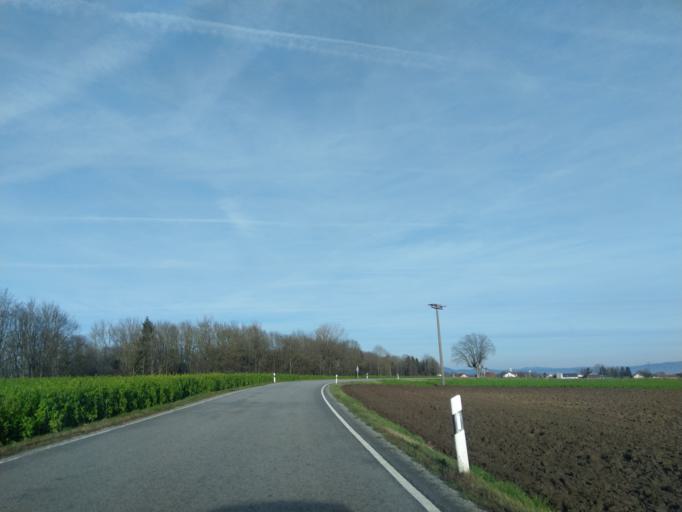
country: DE
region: Bavaria
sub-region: Lower Bavaria
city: Oberporing
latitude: 48.6978
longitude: 12.8133
